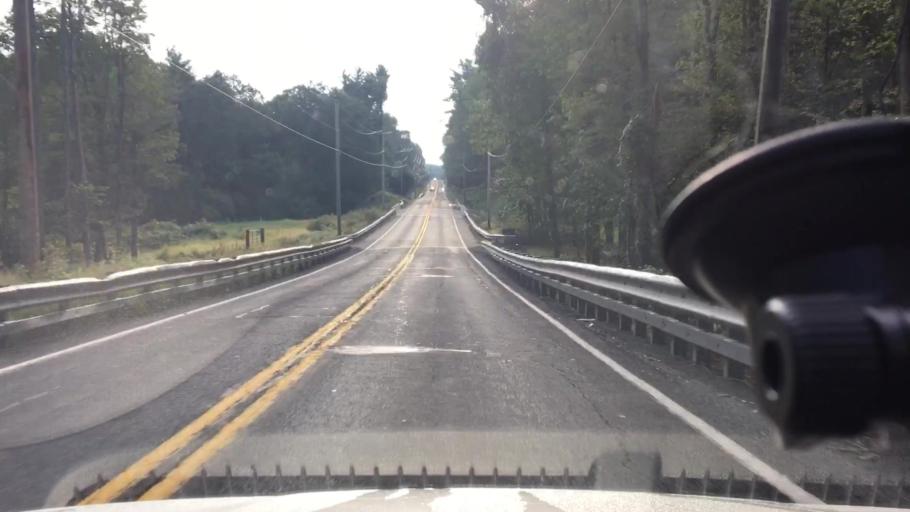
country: US
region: Pennsylvania
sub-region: Monroe County
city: Mount Pocono
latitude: 41.1010
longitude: -75.3480
